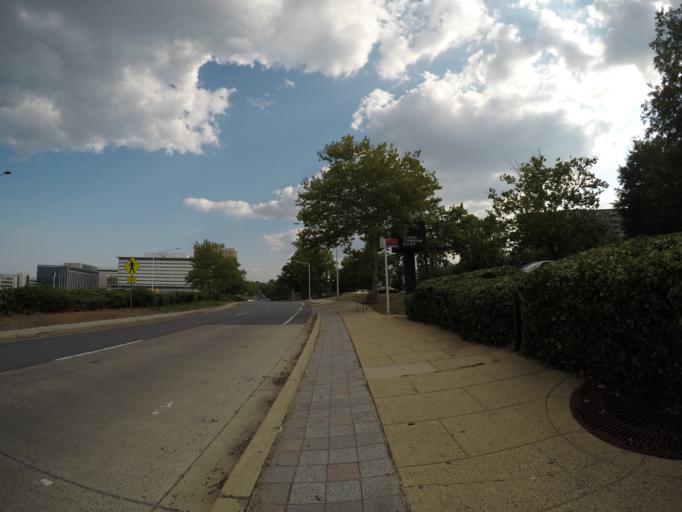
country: US
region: Maryland
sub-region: Prince George's County
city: University Park
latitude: 38.9723
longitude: -76.9537
